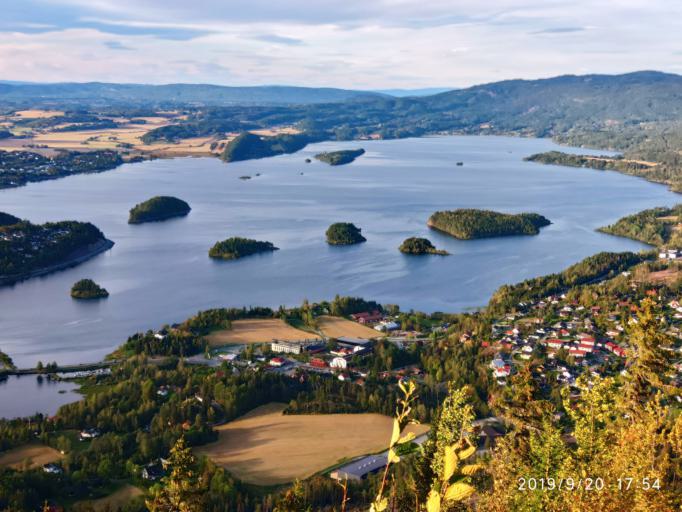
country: NO
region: Buskerud
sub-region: Hole
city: Vik
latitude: 60.0495
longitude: 10.3085
